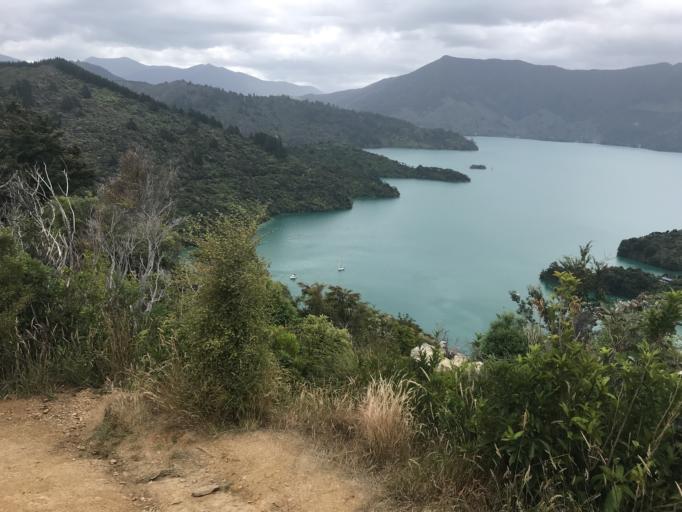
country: NZ
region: Marlborough
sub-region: Marlborough District
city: Picton
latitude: -41.2181
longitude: 173.9755
